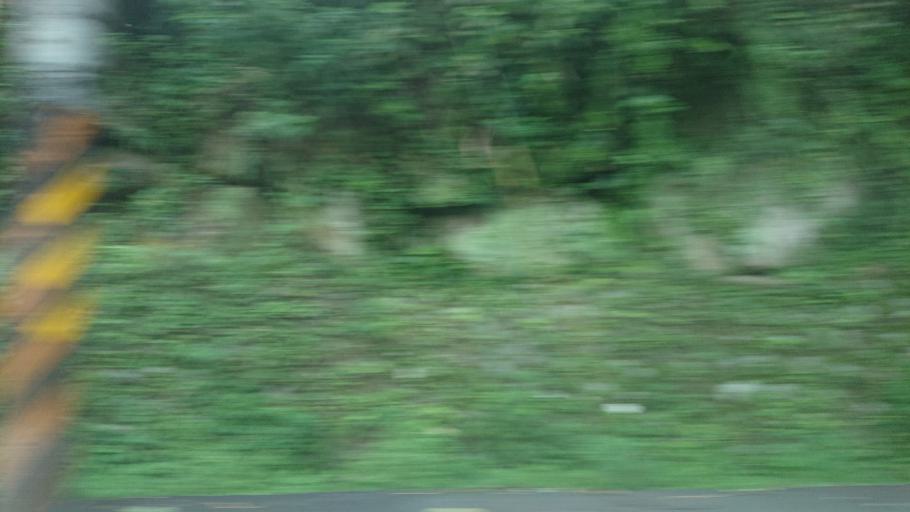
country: TW
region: Taiwan
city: Daxi
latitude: 24.8890
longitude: 121.3772
